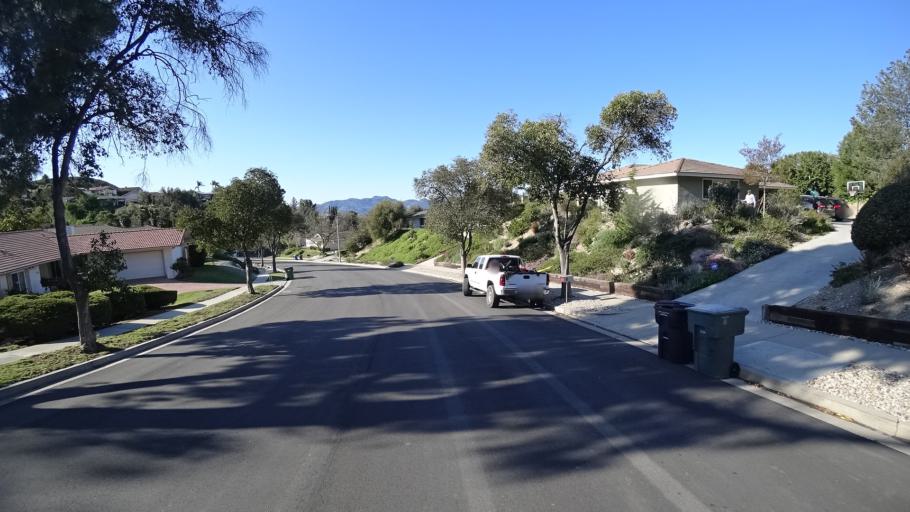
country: US
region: California
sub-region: Ventura County
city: Thousand Oaks
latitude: 34.1963
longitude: -118.8349
